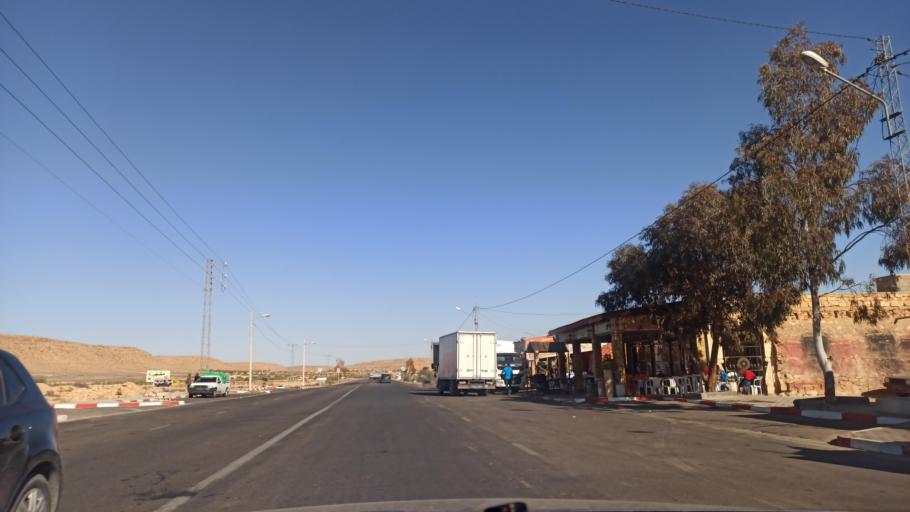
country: TN
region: Sidi Bu Zayd
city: Bi'r al Hufayy
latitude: 34.7051
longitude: 9.0455
